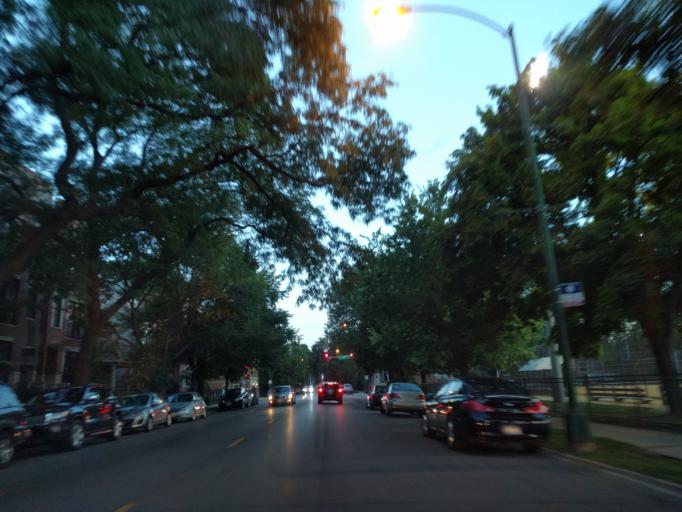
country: US
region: Illinois
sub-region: Cook County
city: Lincolnwood
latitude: 41.9366
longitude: -87.6783
